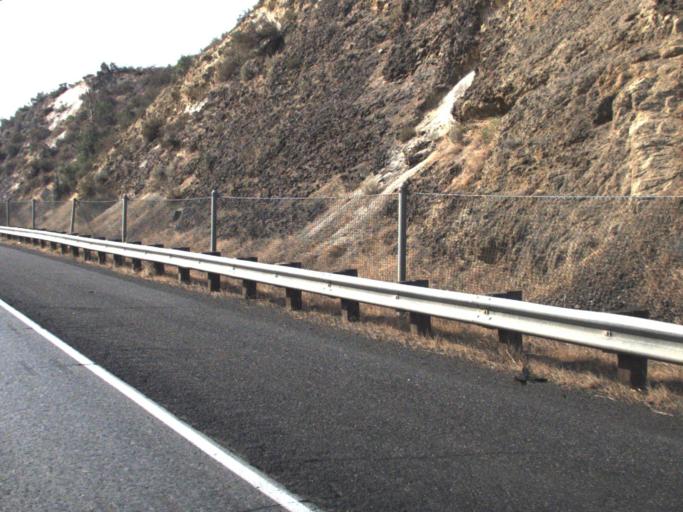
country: US
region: Washington
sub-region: Kittitas County
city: Kittitas
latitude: 46.8806
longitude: -120.4253
